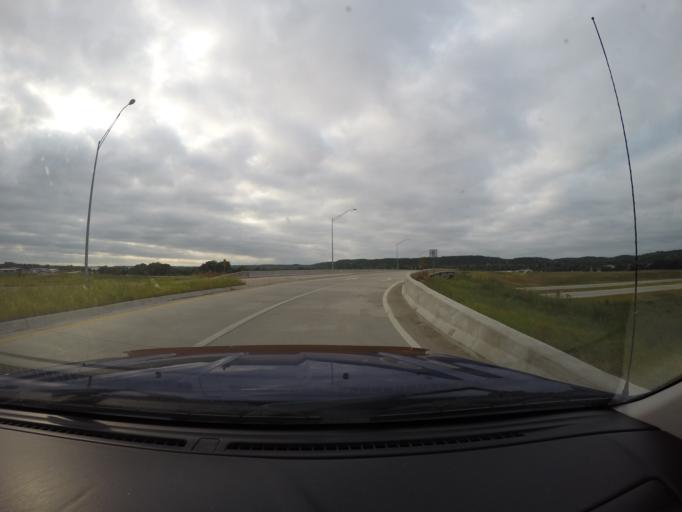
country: US
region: Kansas
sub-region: Riley County
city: Ogden
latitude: 39.1536
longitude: -96.6431
